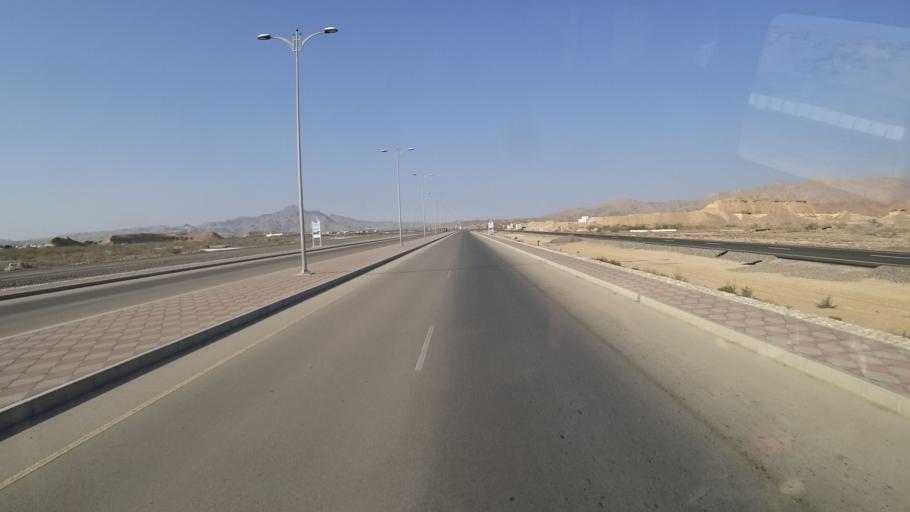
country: OM
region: Ash Sharqiyah
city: Sur
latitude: 22.5874
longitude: 59.4762
